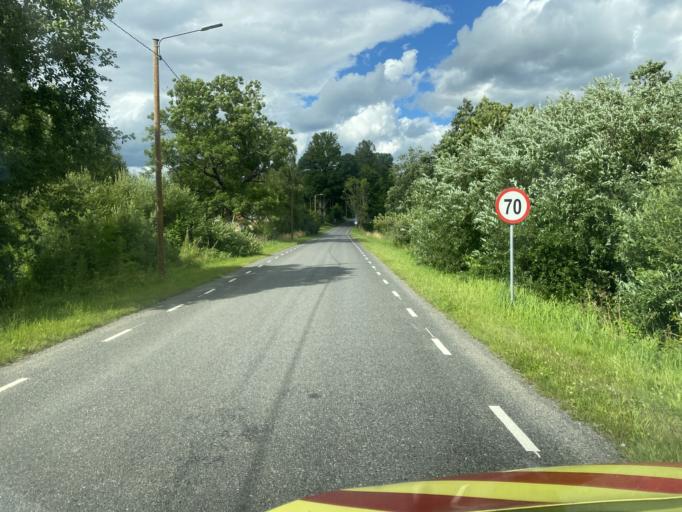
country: EE
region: Viljandimaa
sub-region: Viiratsi vald
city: Viiratsi
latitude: 58.3945
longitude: 25.7631
